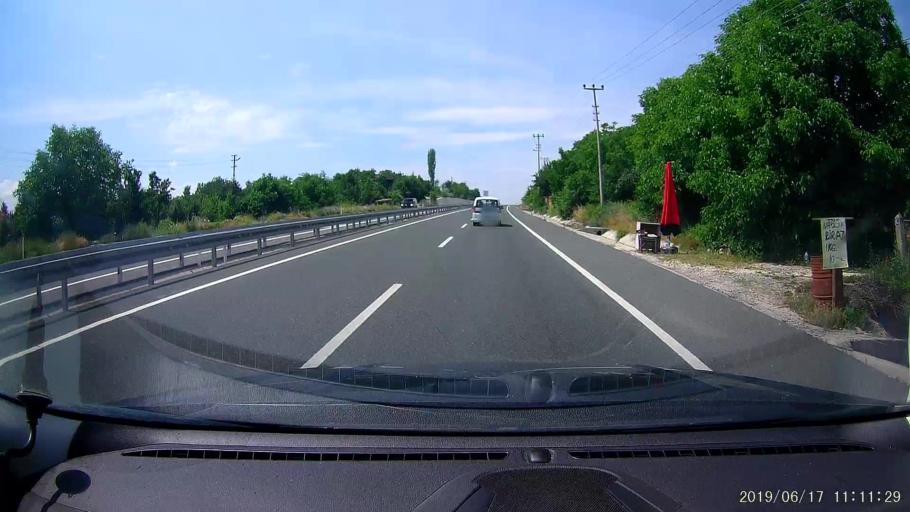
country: TR
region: Kastamonu
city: Tosya
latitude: 40.9861
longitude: 34.0087
